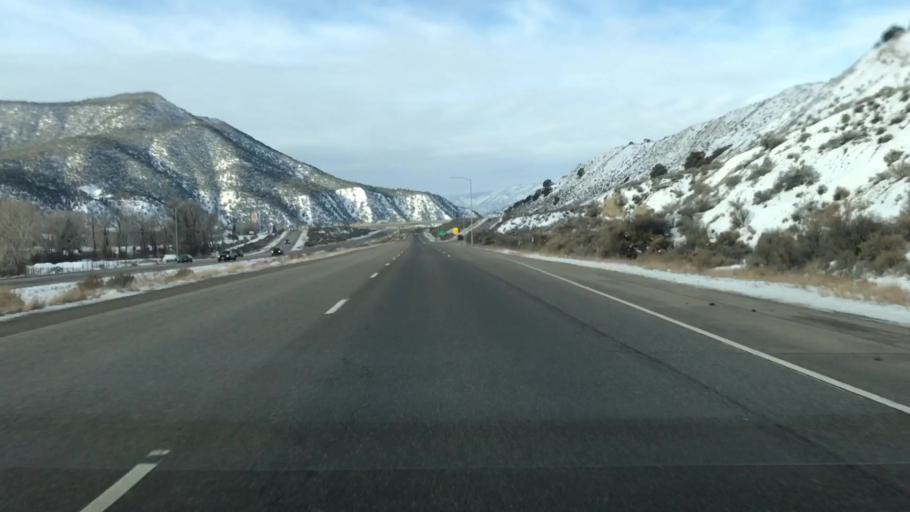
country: US
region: Colorado
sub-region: Eagle County
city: Gypsum
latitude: 39.6530
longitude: -106.9475
